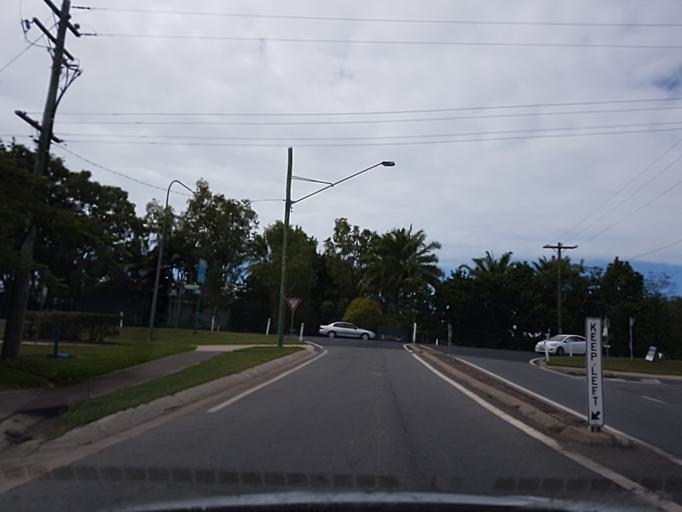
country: AU
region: Queensland
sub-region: Cairns
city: Port Douglas
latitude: -16.4926
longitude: 145.4639
